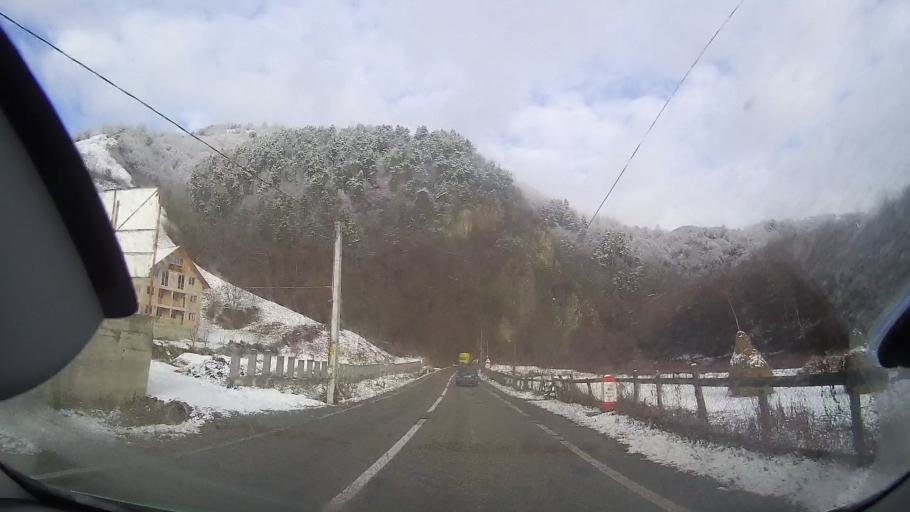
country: RO
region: Alba
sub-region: Oras Baia de Aries
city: Baia de Aries
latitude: 46.3994
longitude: 23.3011
